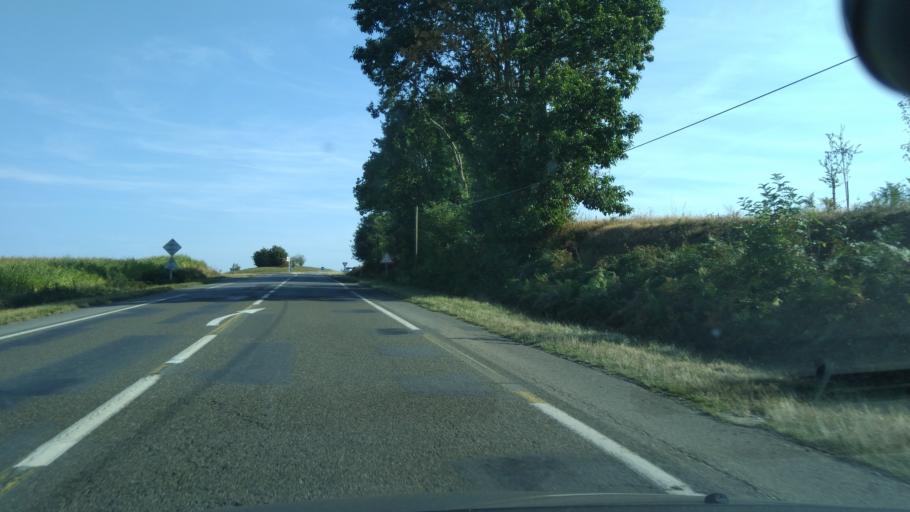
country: FR
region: Pays de la Loire
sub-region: Departement de la Mayenne
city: Entrammes
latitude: 48.0165
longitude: -0.7307
